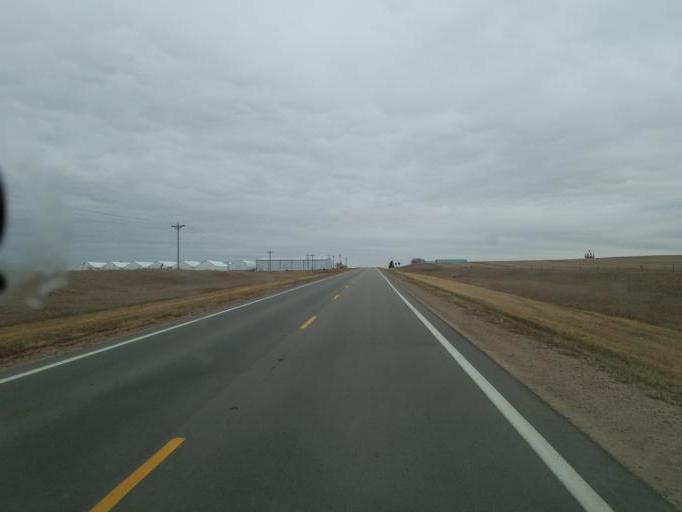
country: US
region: Nebraska
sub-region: Cedar County
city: Hartington
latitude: 42.6126
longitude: -97.2882
